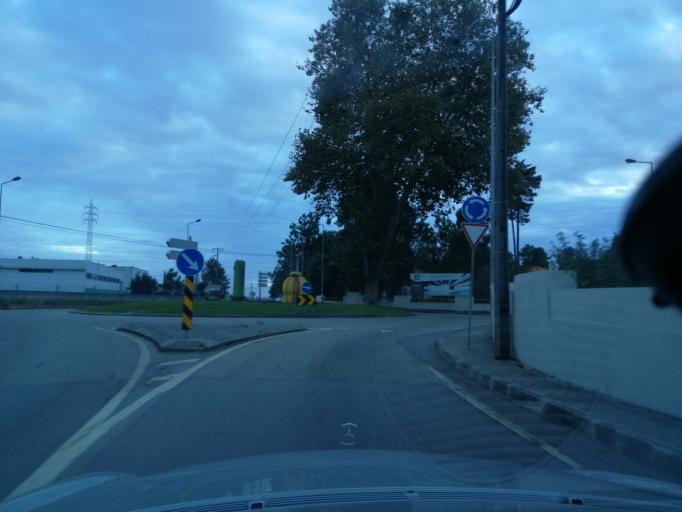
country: PT
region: Aveiro
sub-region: Estarreja
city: Beduido
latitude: 40.7755
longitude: -8.5681
